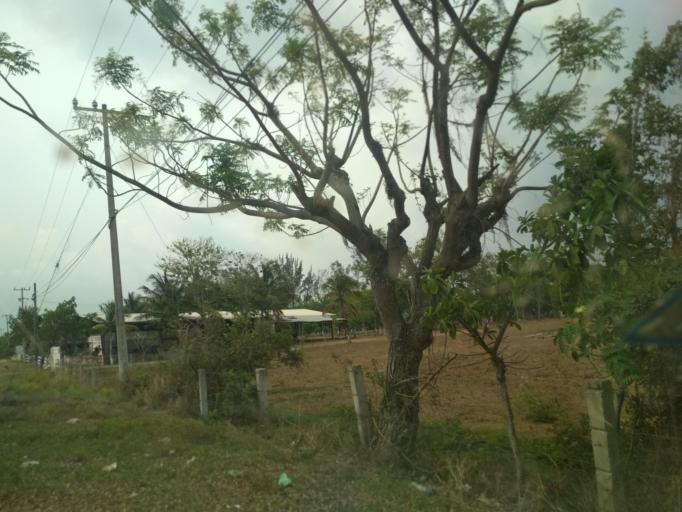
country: MX
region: Veracruz
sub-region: Medellin
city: La Laguna y Monte del Castillo
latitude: 18.9994
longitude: -96.1044
